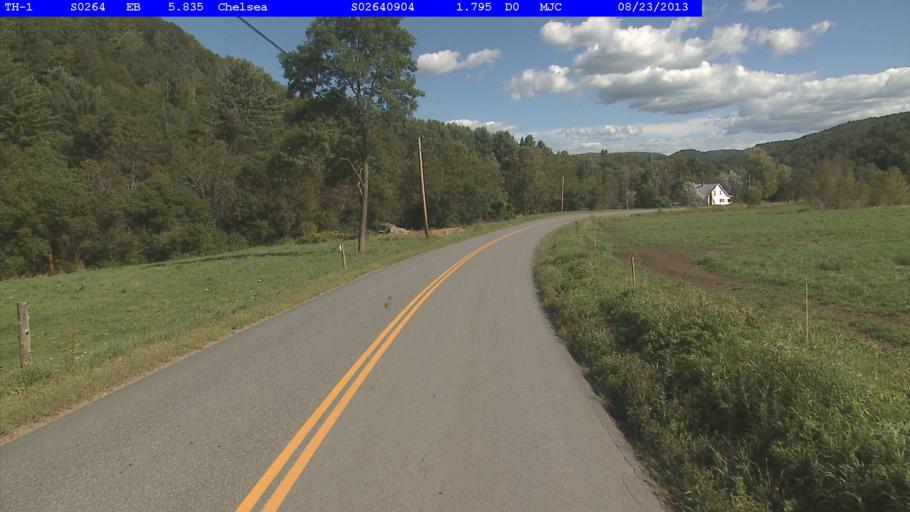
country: US
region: Vermont
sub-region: Orange County
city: Chelsea
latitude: 43.9706
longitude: -72.4789
